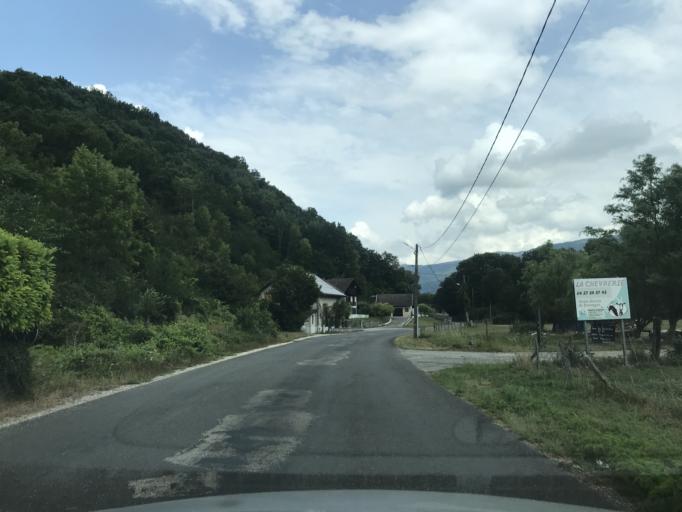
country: FR
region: Rhone-Alpes
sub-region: Departement de l'Ain
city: Culoz
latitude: 45.8258
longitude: 5.8099
